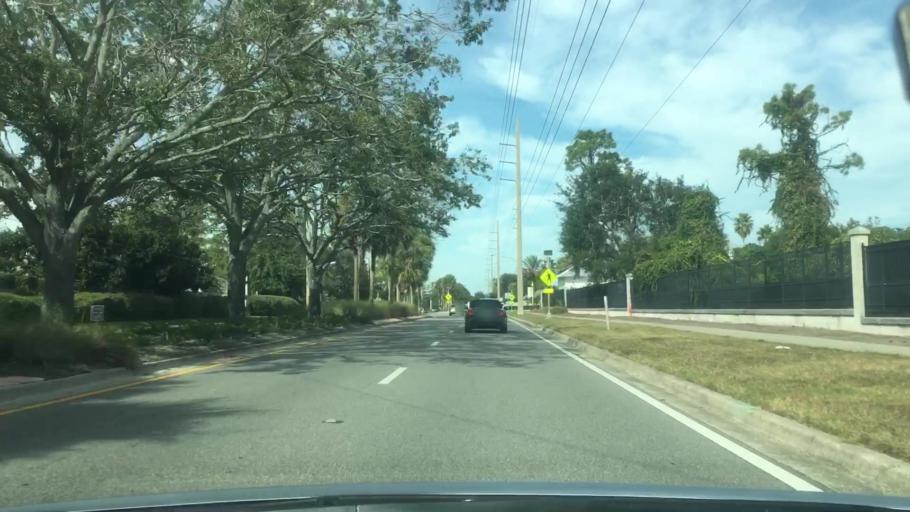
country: US
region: Florida
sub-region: Saint Johns County
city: Ponte Vedra Beach
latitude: 30.2602
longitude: -81.3945
